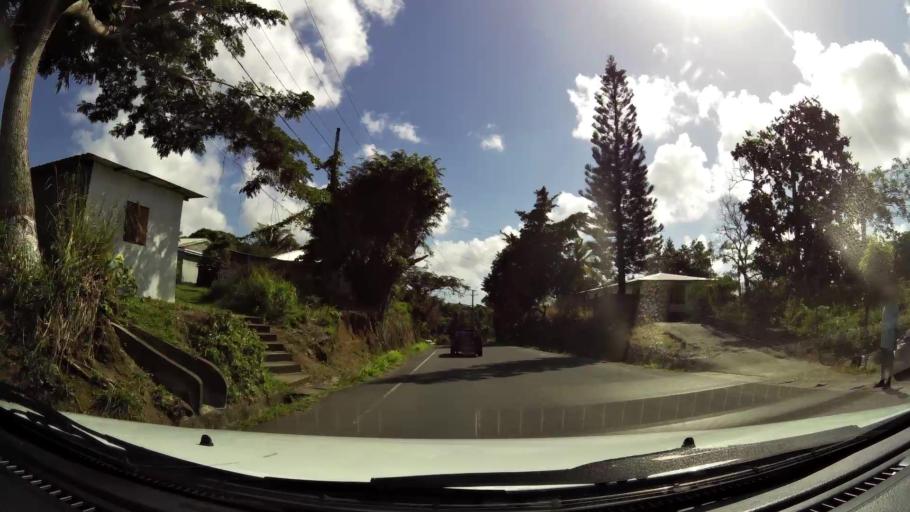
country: LC
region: Choiseul Quarter
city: Choiseul
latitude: 13.7638
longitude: -61.0362
